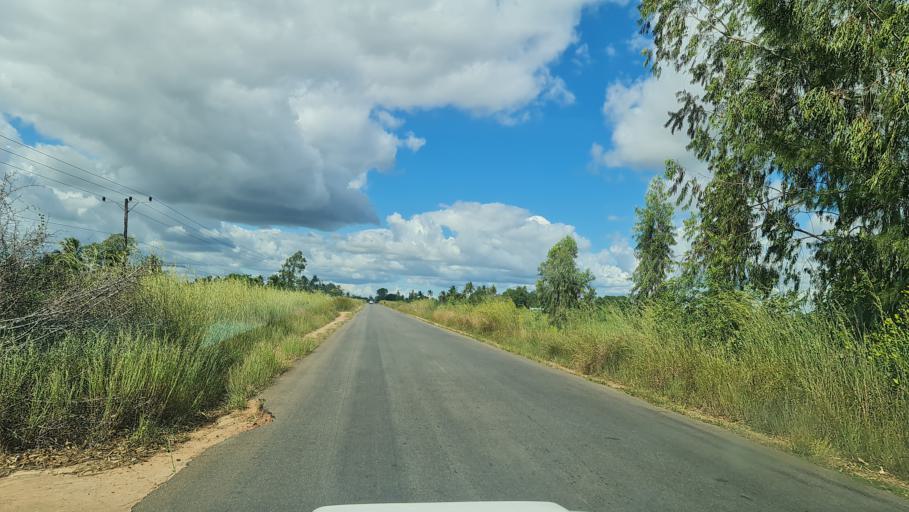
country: MZ
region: Zambezia
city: Quelimane
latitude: -17.5908
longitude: 36.7654
